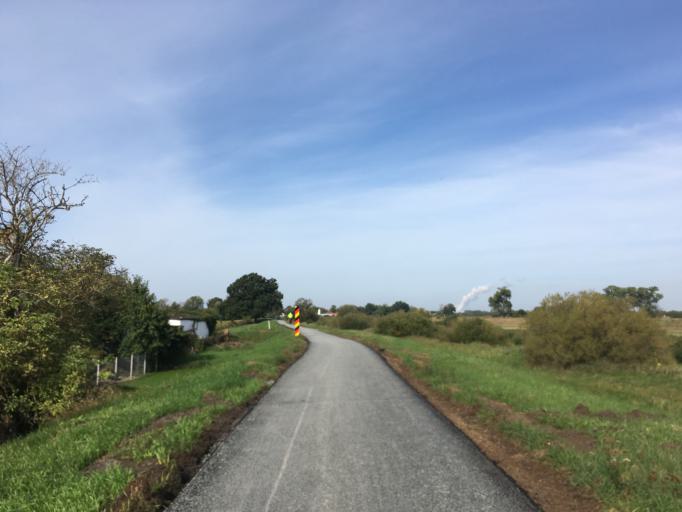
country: DE
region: Brandenburg
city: Forst
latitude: 51.7588
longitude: 14.6598
